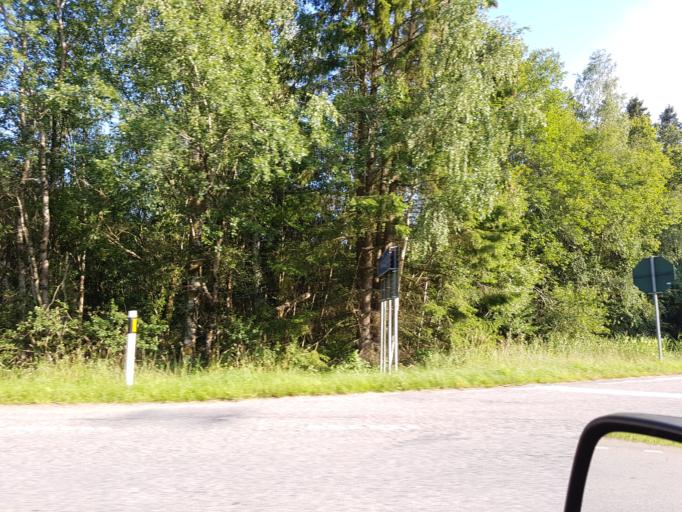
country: SE
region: Vaestra Goetaland
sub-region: Lysekils Kommun
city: Brastad
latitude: 58.4631
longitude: 11.5420
